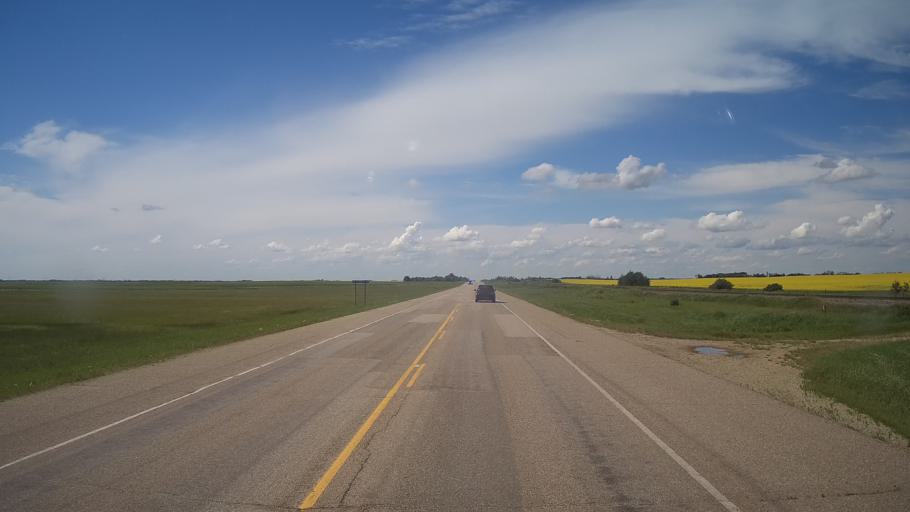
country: CA
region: Saskatchewan
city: Yorkton
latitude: 51.0778
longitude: -102.2404
